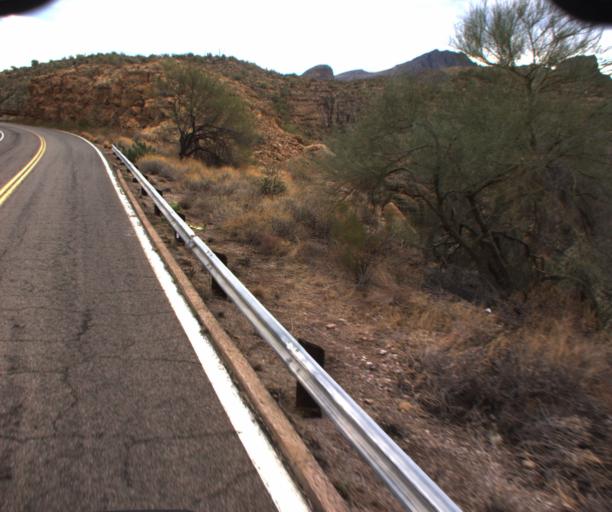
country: US
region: Arizona
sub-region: Pinal County
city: Apache Junction
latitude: 33.5326
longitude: -111.3666
